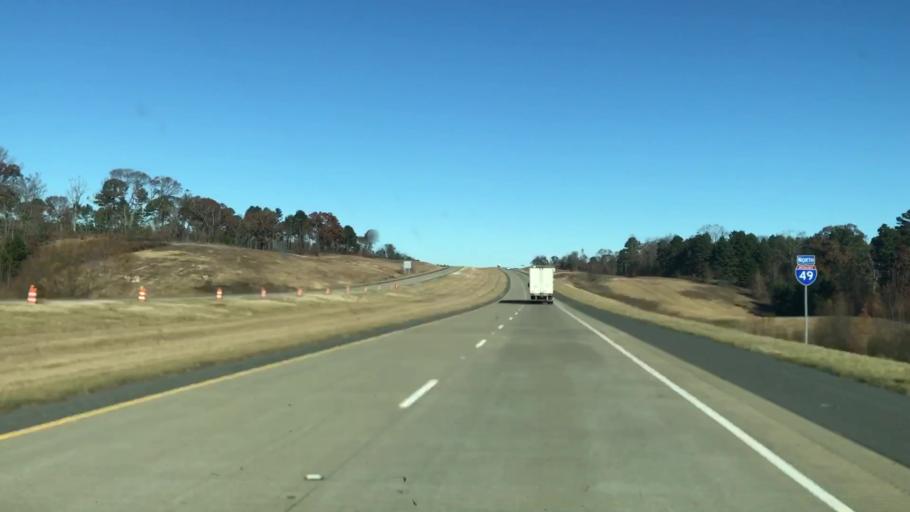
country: US
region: Louisiana
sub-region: Caddo Parish
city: Vivian
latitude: 32.9513
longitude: -93.8994
